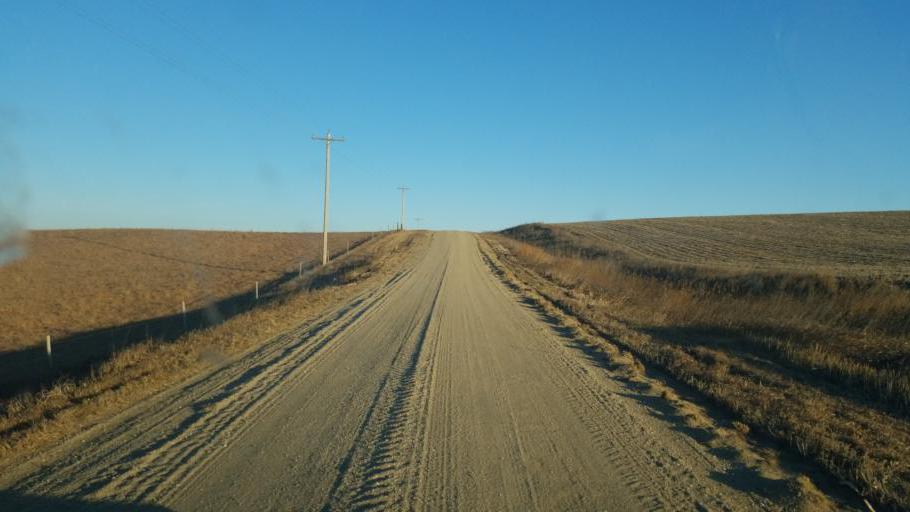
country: US
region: Nebraska
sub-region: Knox County
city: Center
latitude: 42.5871
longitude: -97.7790
